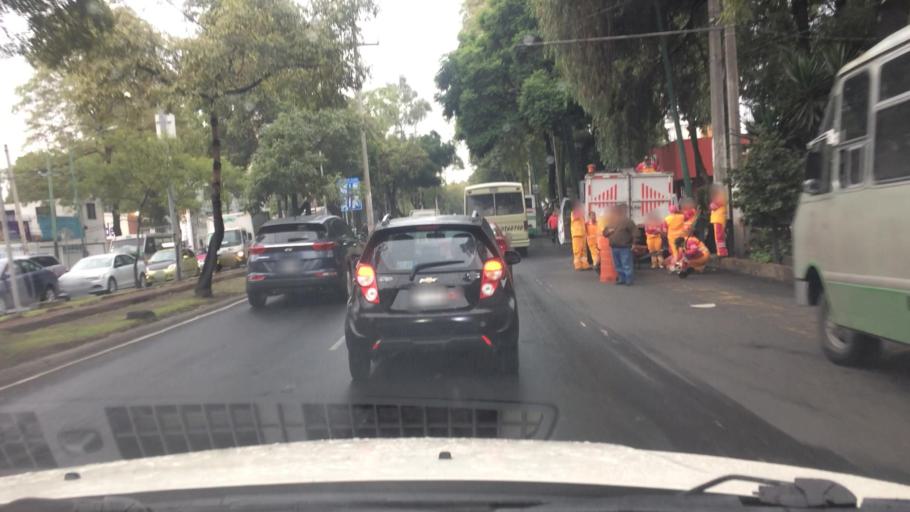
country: MX
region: Mexico City
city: Coyoacan
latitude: 19.3410
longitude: -99.1367
